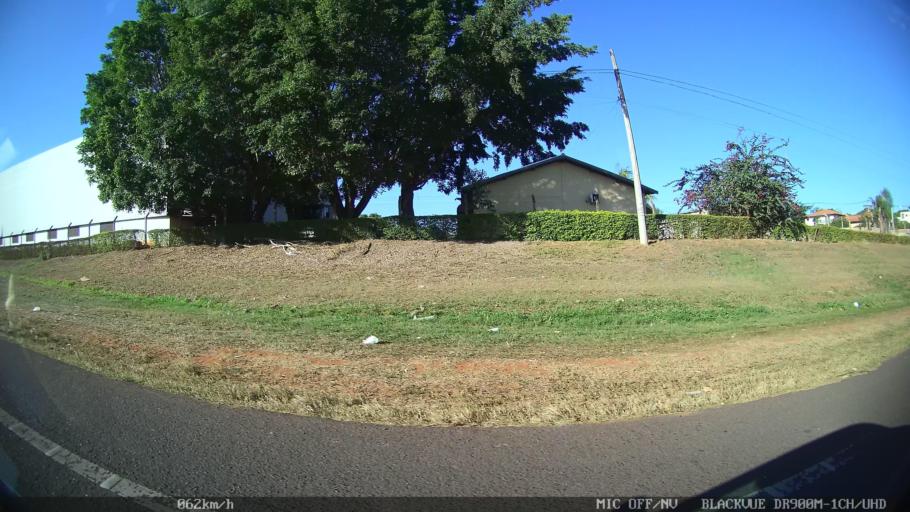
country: BR
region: Sao Paulo
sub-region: Olimpia
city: Olimpia
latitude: -20.7203
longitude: -48.9062
